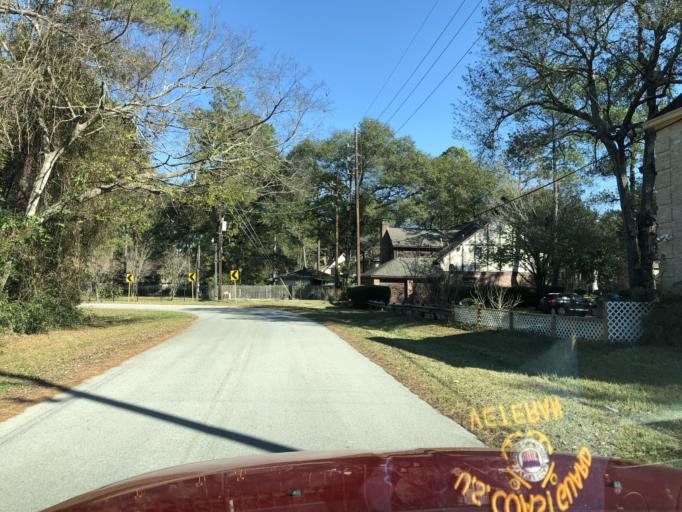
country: US
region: Texas
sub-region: Harris County
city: Tomball
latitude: 30.0292
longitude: -95.5416
